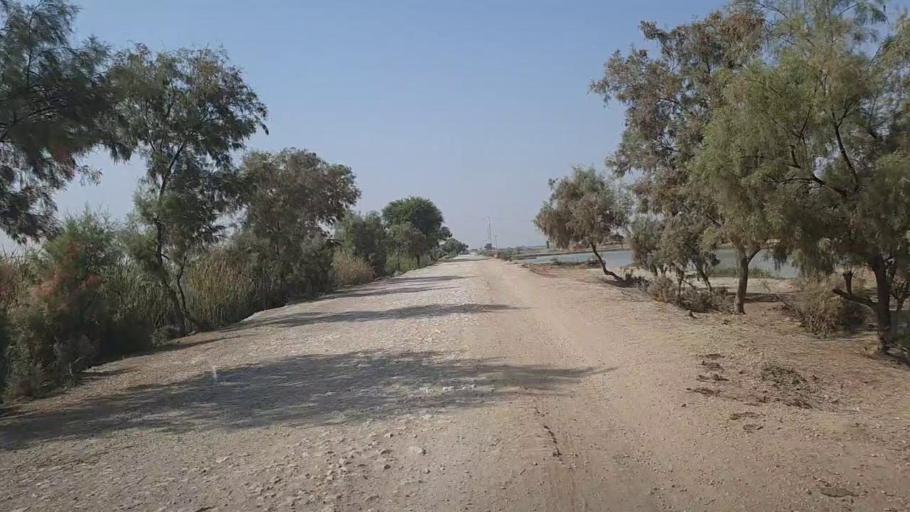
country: PK
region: Sindh
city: Kandhkot
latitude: 28.4051
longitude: 69.2553
